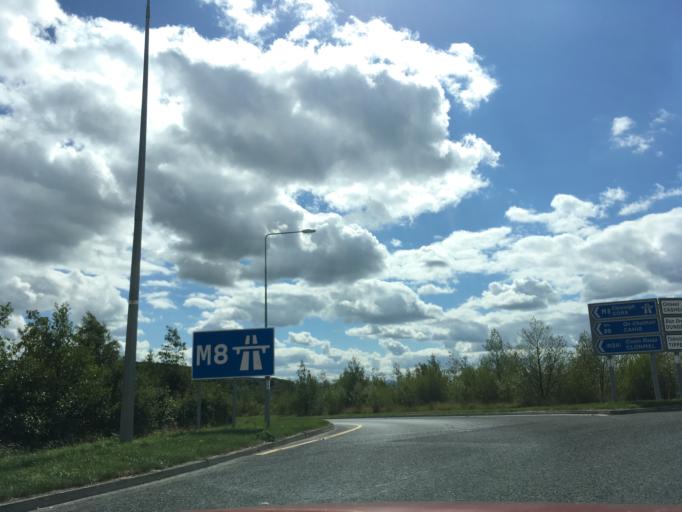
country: IE
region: Munster
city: Cashel
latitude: 52.5429
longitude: -7.8634
